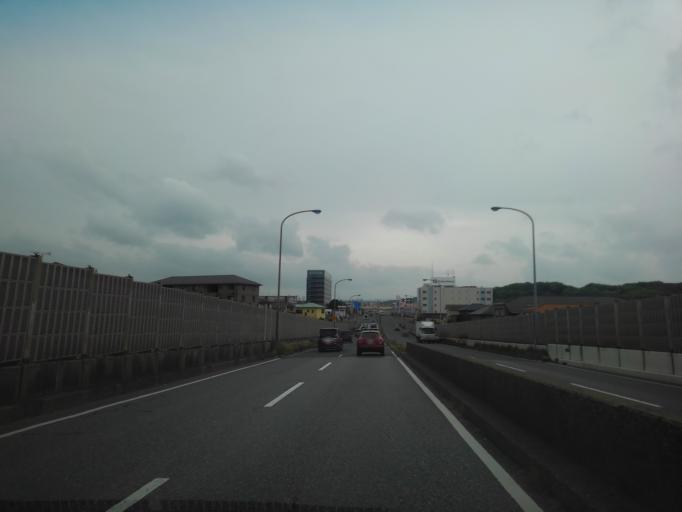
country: JP
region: Chiba
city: Kisarazu
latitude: 35.3851
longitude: 139.9417
